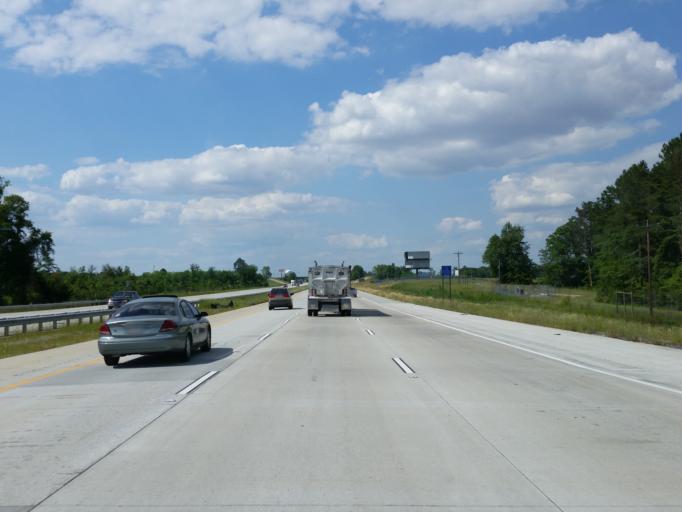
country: US
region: Georgia
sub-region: Dooly County
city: Vienna
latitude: 32.0787
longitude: -83.7632
